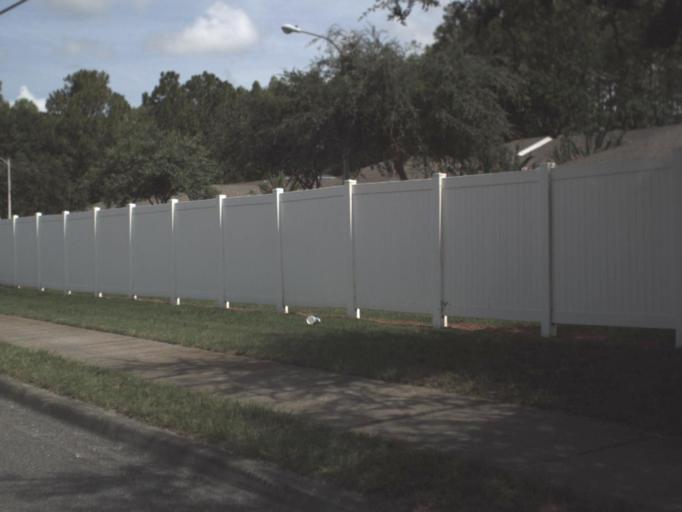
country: US
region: Florida
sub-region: Pasco County
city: Bayonet Point
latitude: 28.3378
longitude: -82.6104
